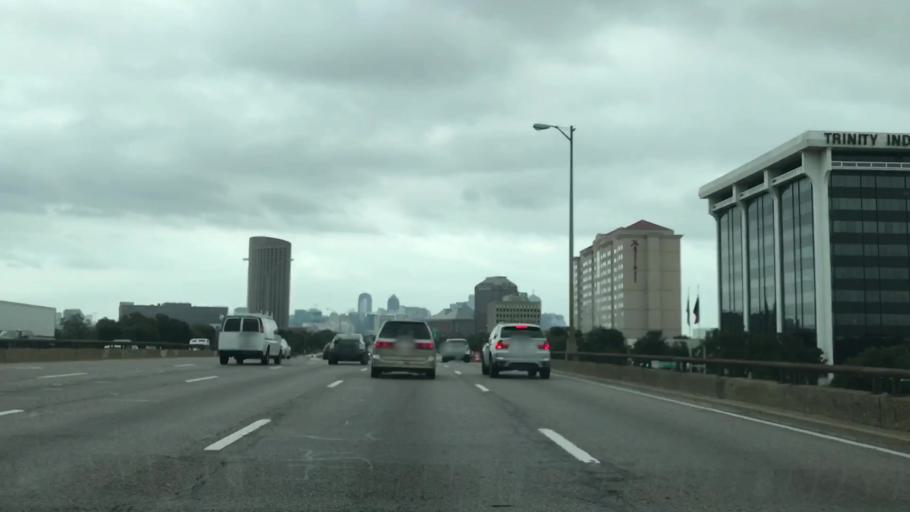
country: US
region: Texas
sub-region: Dallas County
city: Dallas
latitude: 32.8068
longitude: -96.8411
